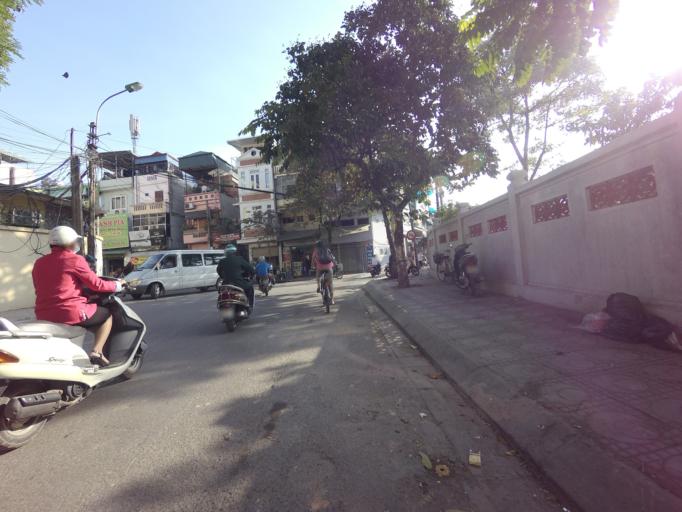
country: VN
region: Ha Noi
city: Hanoi
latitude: 21.0379
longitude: 105.8297
